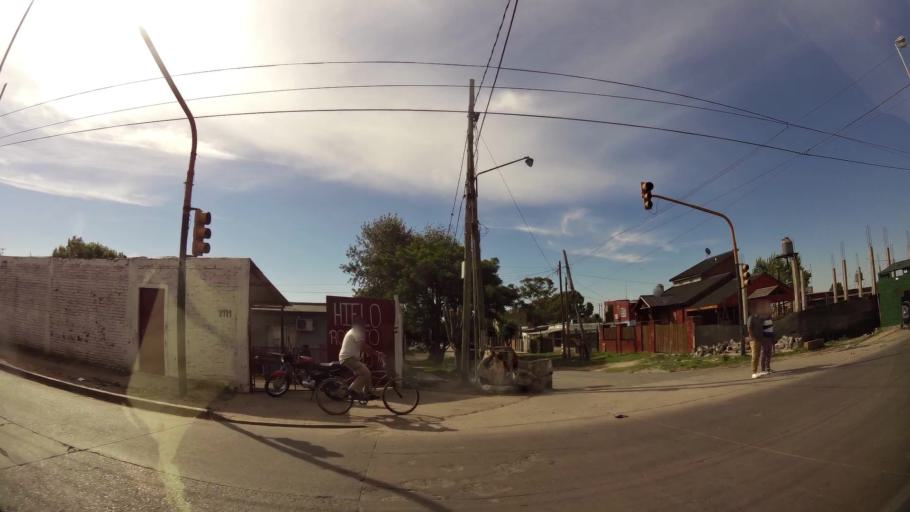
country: AR
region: Buenos Aires
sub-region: Partido de Almirante Brown
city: Adrogue
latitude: -34.8142
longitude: -58.3536
